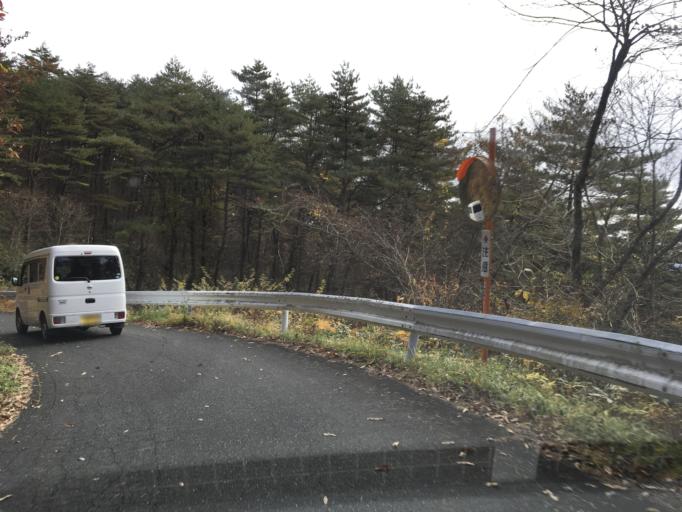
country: JP
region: Iwate
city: Mizusawa
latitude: 39.1284
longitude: 141.3100
